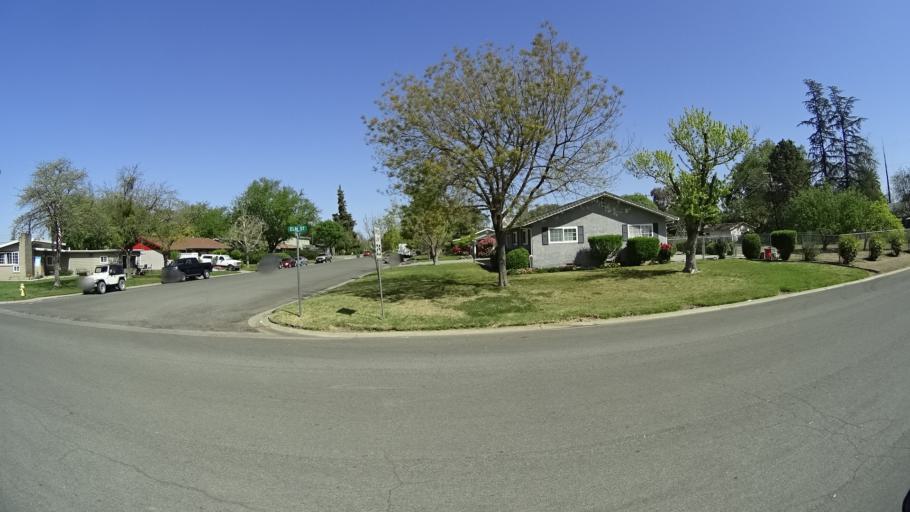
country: US
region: California
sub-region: Glenn County
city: Willows
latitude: 39.5127
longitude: -122.1980
